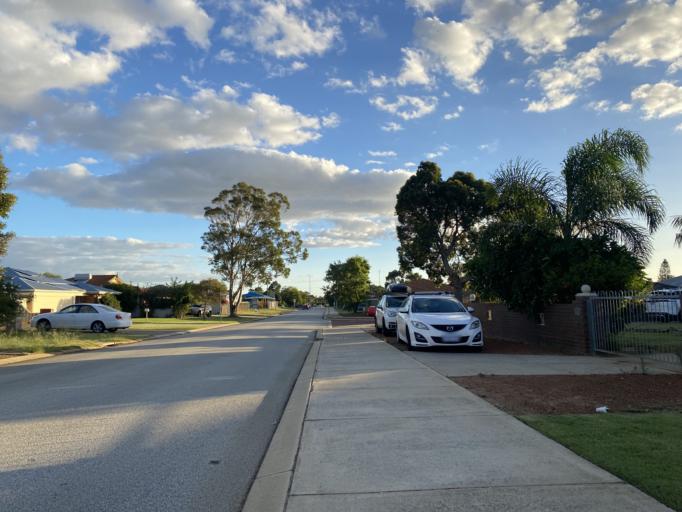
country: AU
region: Western Australia
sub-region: Kalamunda
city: Maida Vale
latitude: -31.9708
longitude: 116.0052
